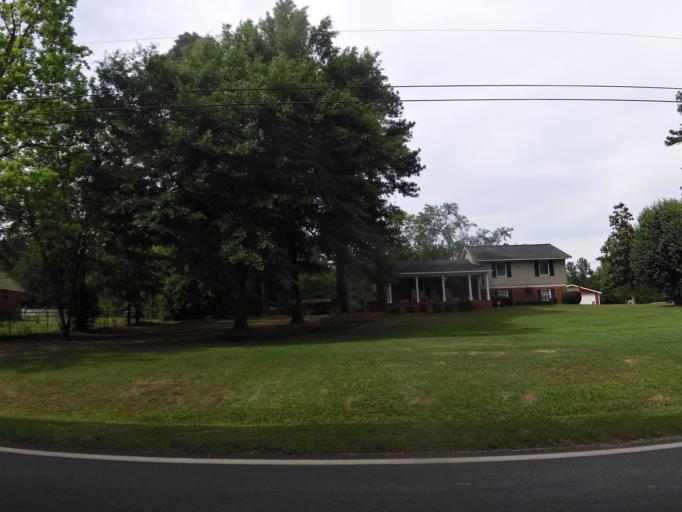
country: US
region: Georgia
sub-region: McDuffie County
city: Thomson
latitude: 33.5403
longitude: -82.5062
